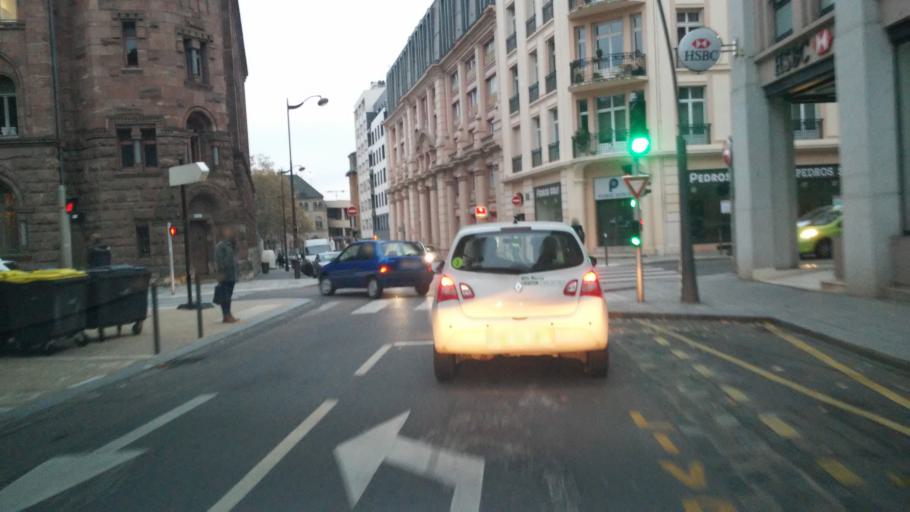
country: FR
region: Lorraine
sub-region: Departement de la Moselle
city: Metz
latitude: 49.1103
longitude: 6.1739
